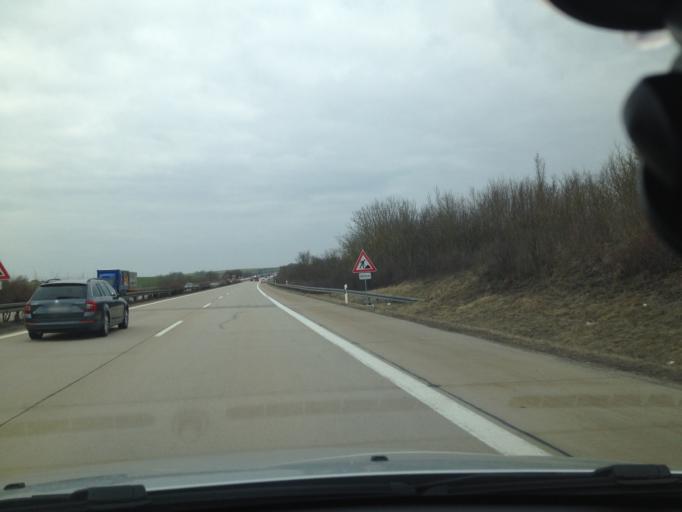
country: DE
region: Bavaria
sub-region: Regierungsbezirk Mittelfranken
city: Diebach
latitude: 49.2962
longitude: 10.2151
